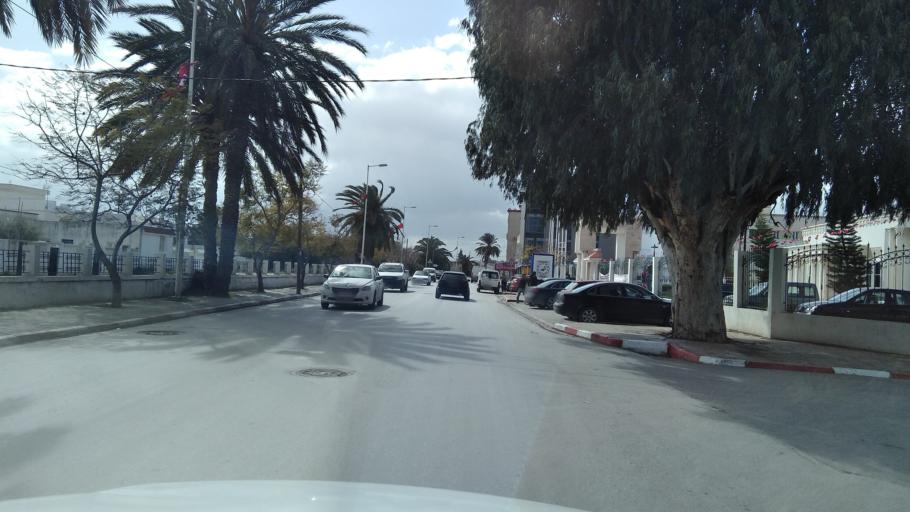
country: TN
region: Bin 'Arus
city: Ben Arous
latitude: 36.7488
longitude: 10.2252
